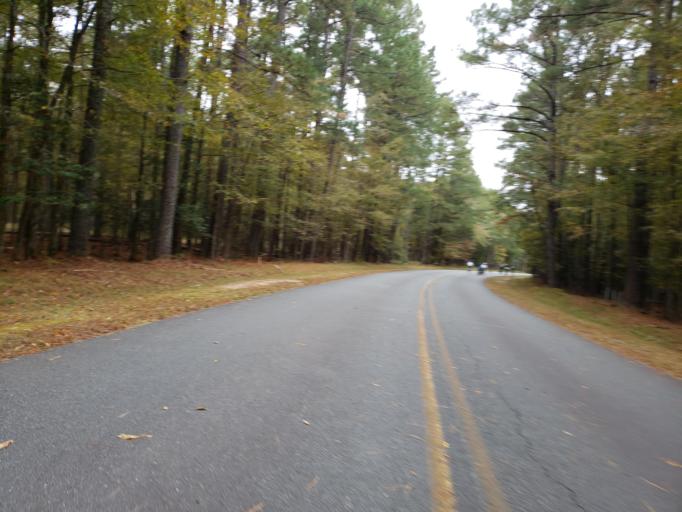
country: US
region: North Carolina
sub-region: Chatham County
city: Fearrington Village
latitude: 35.7497
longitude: -79.0404
